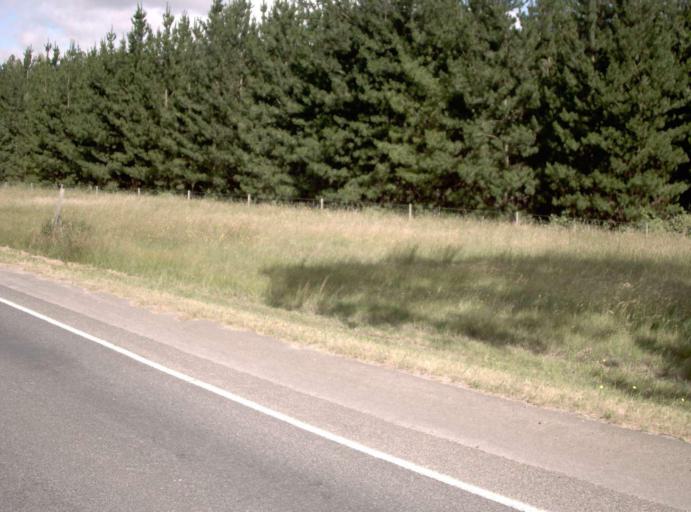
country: AU
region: Victoria
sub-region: Latrobe
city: Traralgon
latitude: -38.1863
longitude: 146.4736
